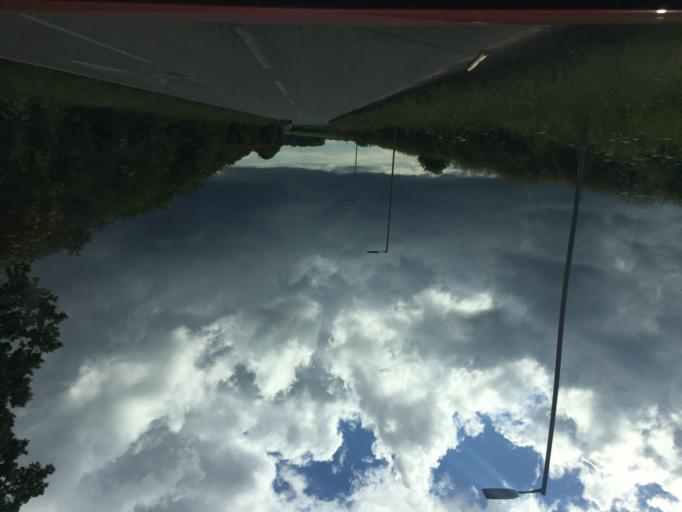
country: GB
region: England
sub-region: Hertfordshire
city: Redbourn
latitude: 51.8365
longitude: -0.3958
